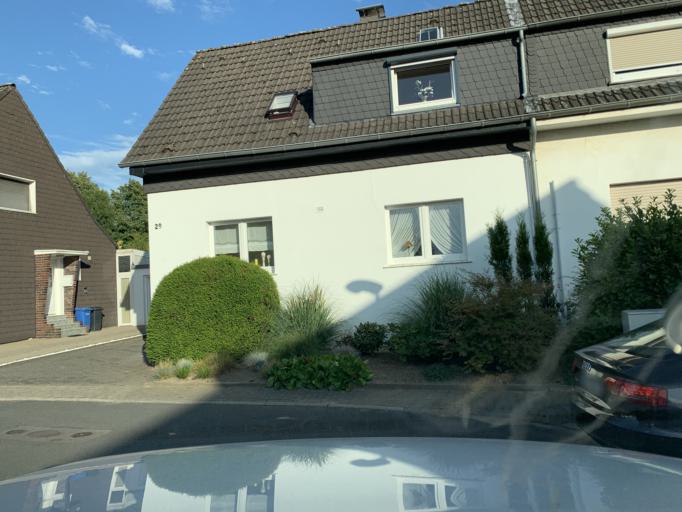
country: DE
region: North Rhine-Westphalia
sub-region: Regierungsbezirk Dusseldorf
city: Oberhausen
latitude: 51.4625
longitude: 6.9205
